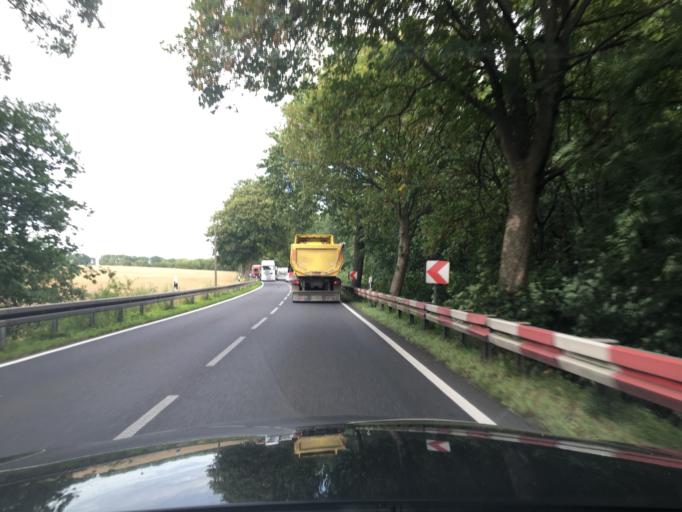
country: DE
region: Brandenburg
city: Gransee
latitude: 52.9103
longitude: 13.1587
